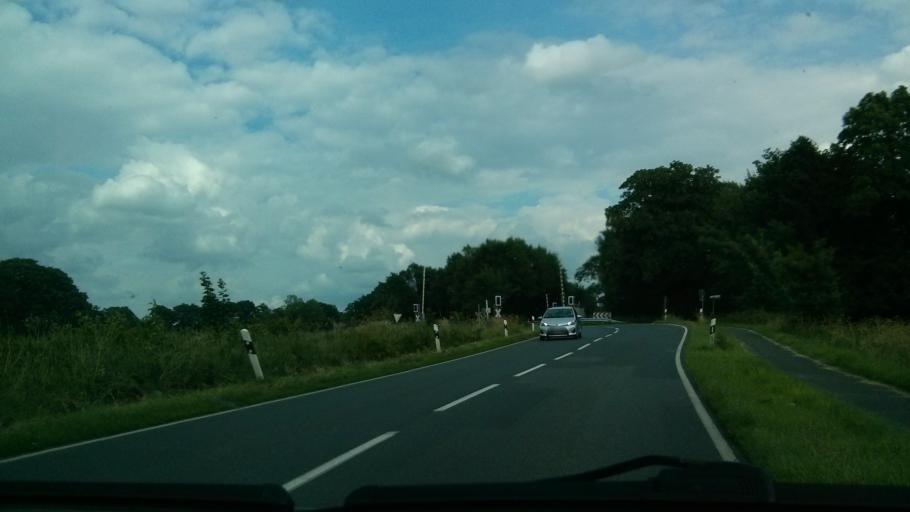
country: DE
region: Lower Saxony
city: Ringstedt
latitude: 53.5103
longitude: 8.8280
